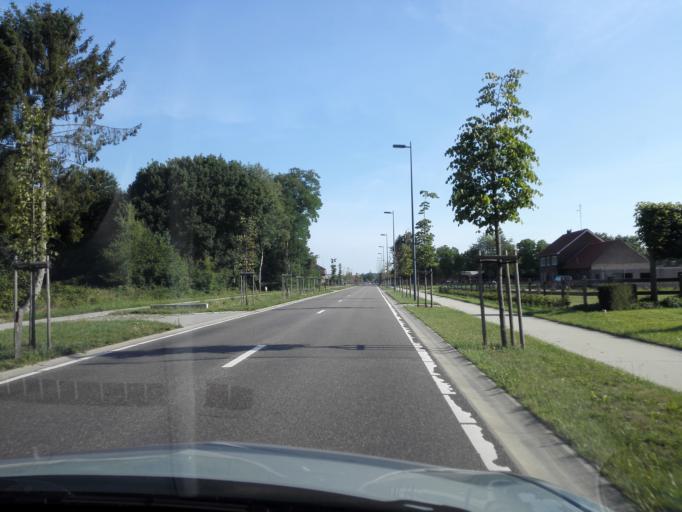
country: BE
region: Flanders
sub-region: Provincie Limburg
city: Opglabbeek
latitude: 51.0790
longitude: 5.5869
